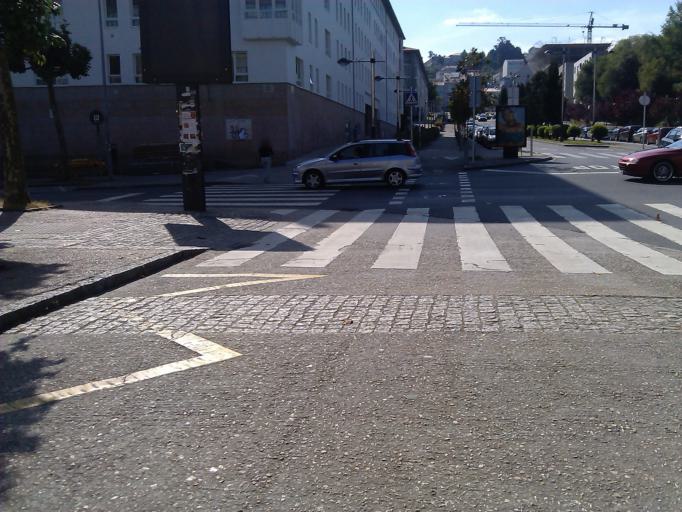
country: ES
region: Galicia
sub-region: Provincia da Coruna
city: Santiago de Compostela
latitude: 42.8830
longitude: -8.5292
